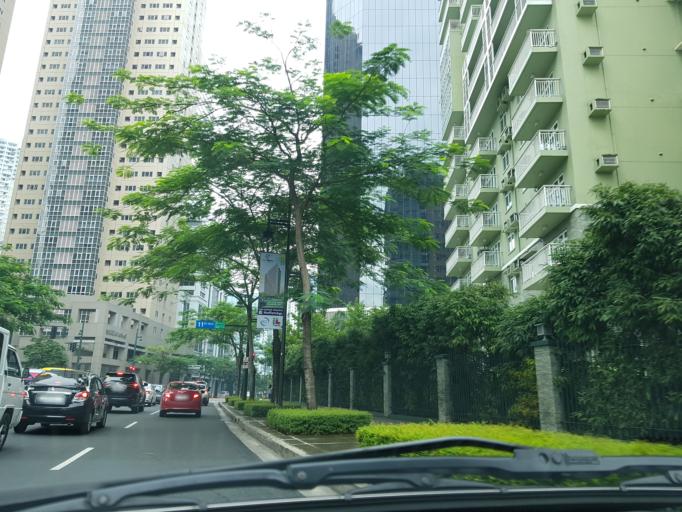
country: PH
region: Metro Manila
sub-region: Makati City
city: Makati City
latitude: 14.5473
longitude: 121.0530
